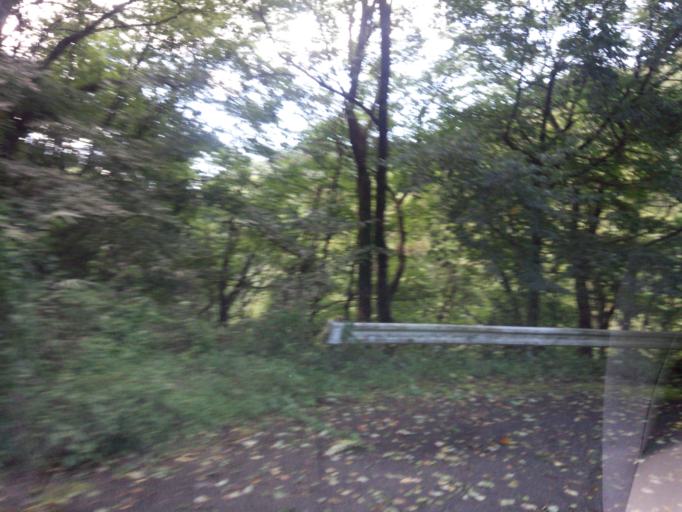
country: JP
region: Gunma
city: Nakanojomachi
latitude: 36.6974
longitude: 138.7745
